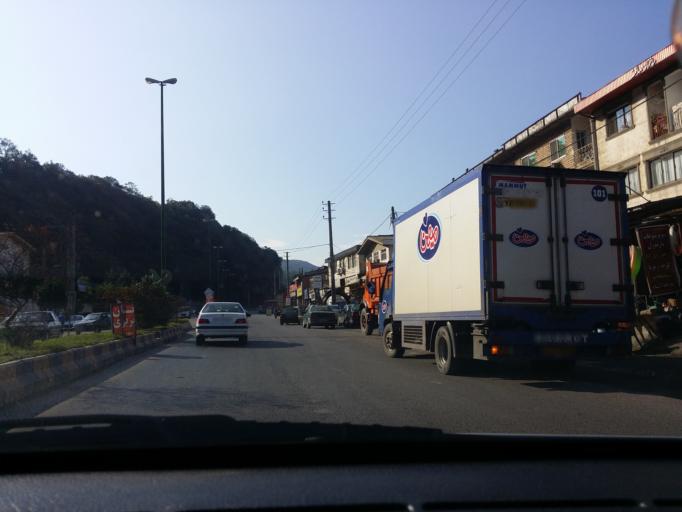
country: IR
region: Mazandaran
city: Chalus
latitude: 36.6424
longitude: 51.4123
